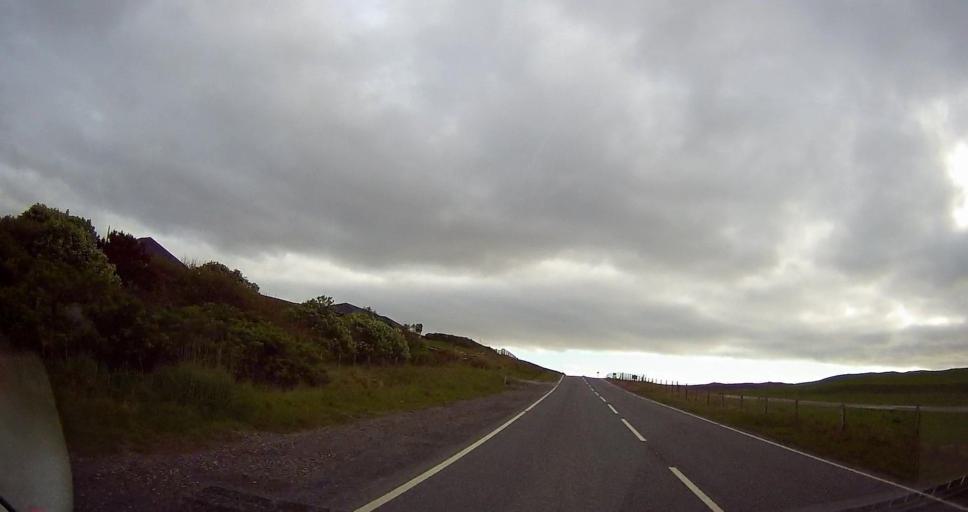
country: GB
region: Scotland
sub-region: Shetland Islands
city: Lerwick
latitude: 60.4312
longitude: -1.2971
